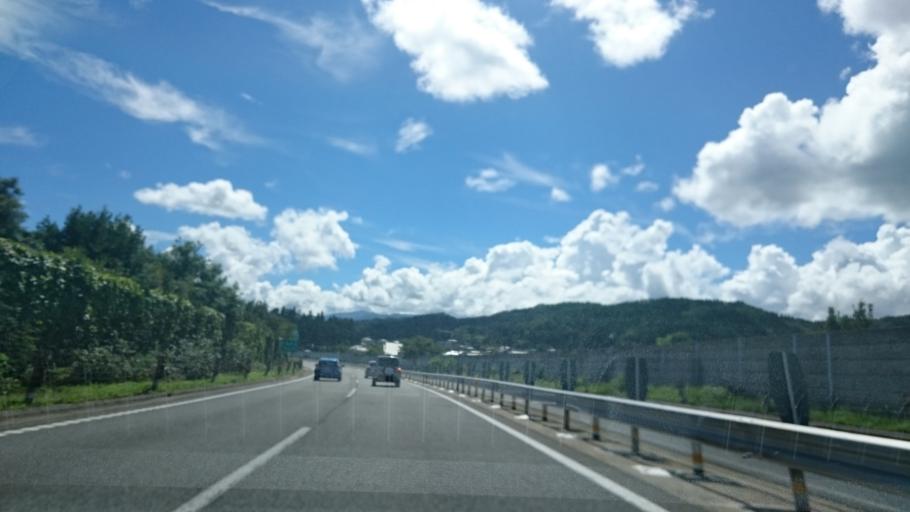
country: JP
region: Nagano
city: Iida
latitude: 35.4799
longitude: 137.7627
